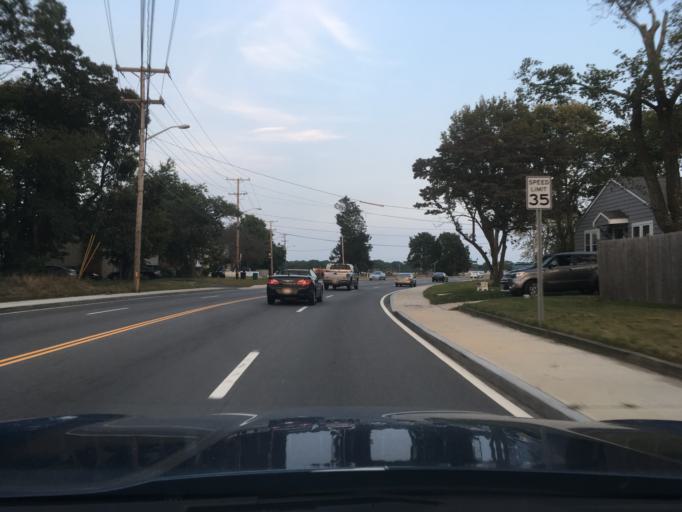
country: US
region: Rhode Island
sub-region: Kent County
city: Warwick
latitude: 41.7108
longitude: -71.4438
